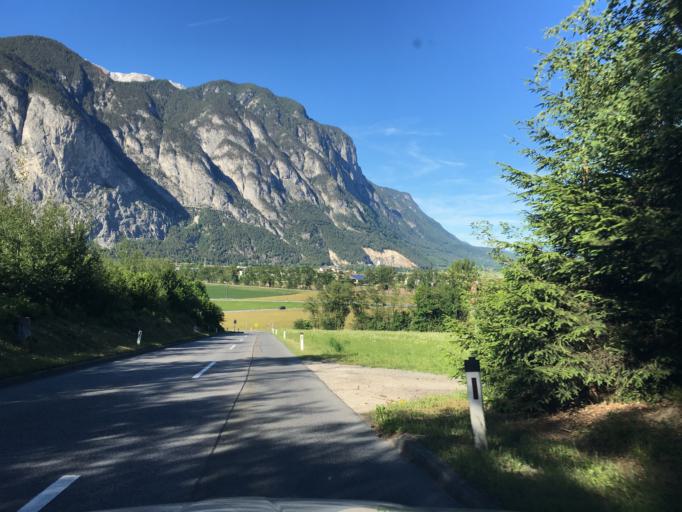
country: AT
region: Tyrol
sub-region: Politischer Bezirk Innsbruck Land
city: Kematen in Tirol
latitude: 47.2538
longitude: 11.2603
